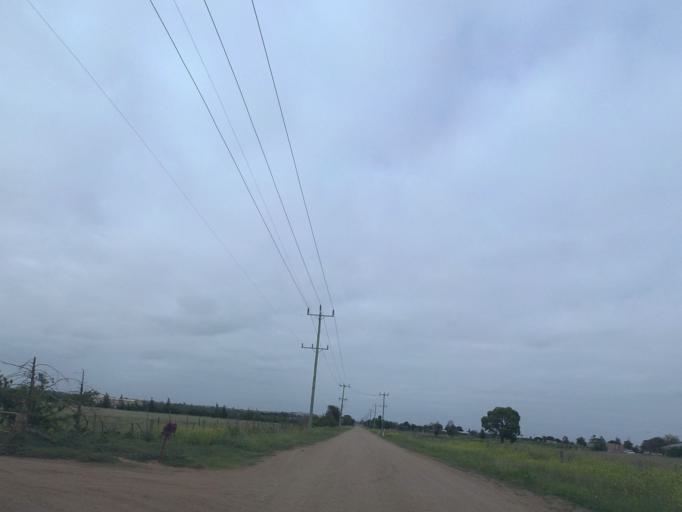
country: AU
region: Victoria
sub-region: Melton
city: Kurunjang
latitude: -37.6937
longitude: 144.6225
